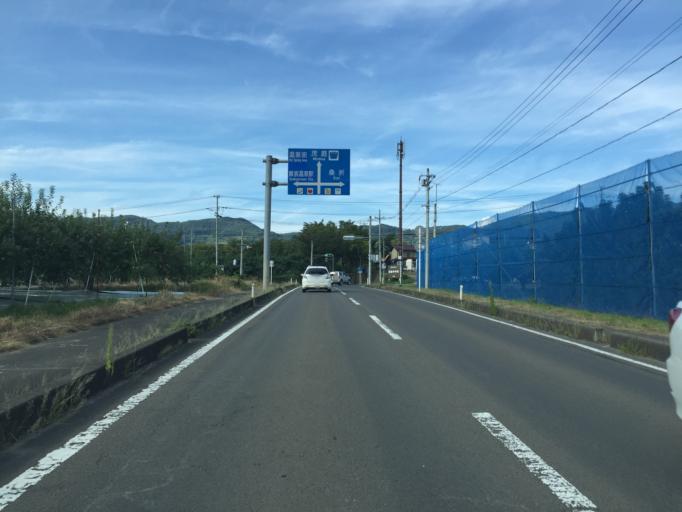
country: JP
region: Fukushima
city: Fukushima-shi
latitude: 37.8287
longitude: 140.4660
